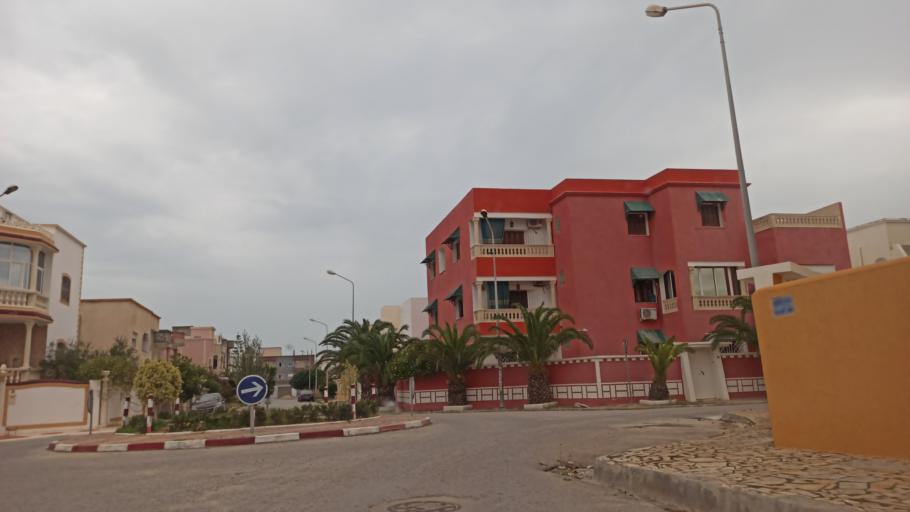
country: TN
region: Tunis
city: Hammam-Lif
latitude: 36.7070
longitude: 10.4142
